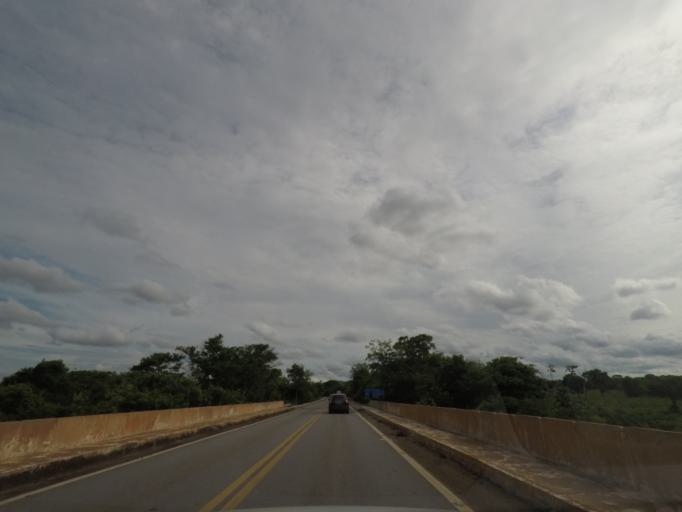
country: BR
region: Goias
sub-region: Uruacu
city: Uruacu
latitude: -14.7442
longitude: -49.0694
